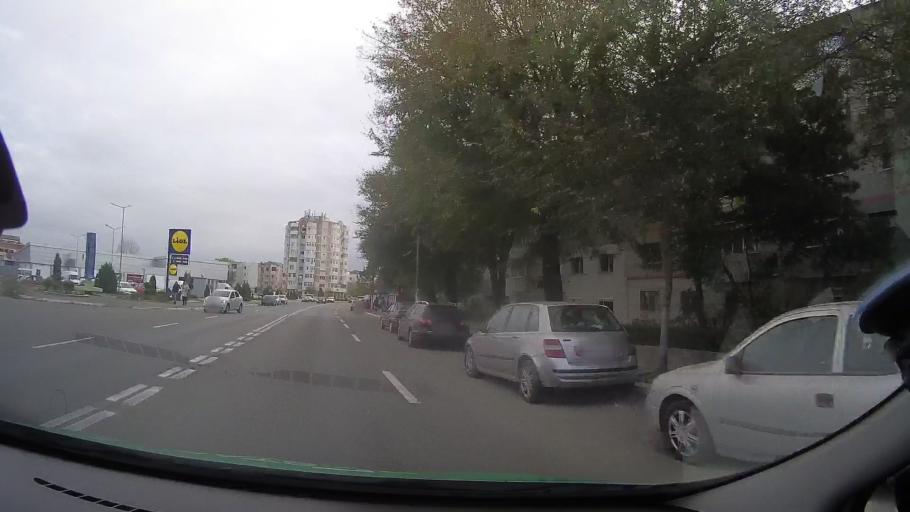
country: RO
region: Constanta
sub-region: Municipiul Medgidia
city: Medgidia
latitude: 44.2626
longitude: 28.2615
